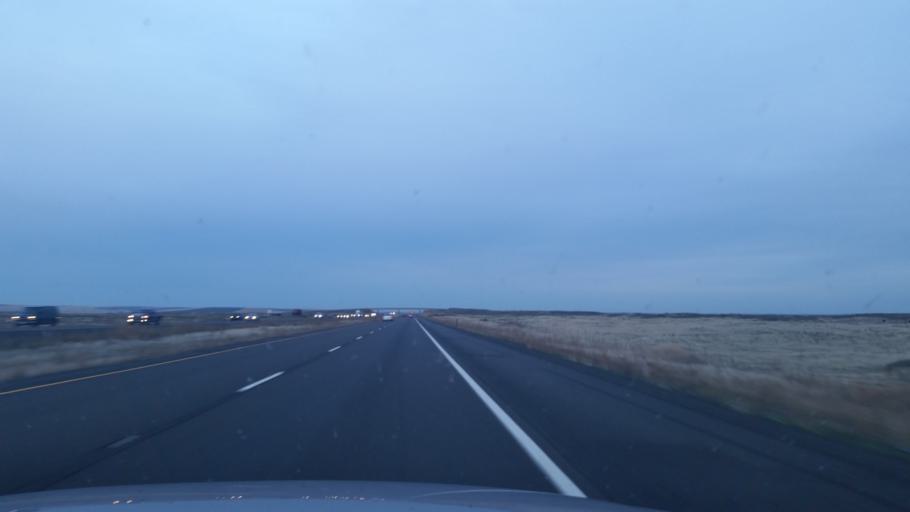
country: US
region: Washington
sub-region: Adams County
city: Ritzville
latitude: 47.2299
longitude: -118.1635
